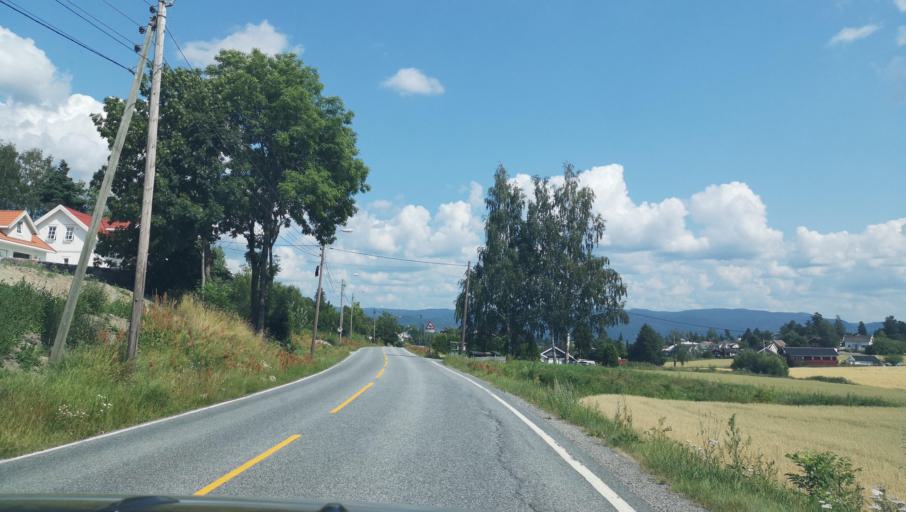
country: NO
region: Buskerud
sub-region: Ovre Eiker
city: Hokksund
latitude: 59.7311
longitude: 9.8458
